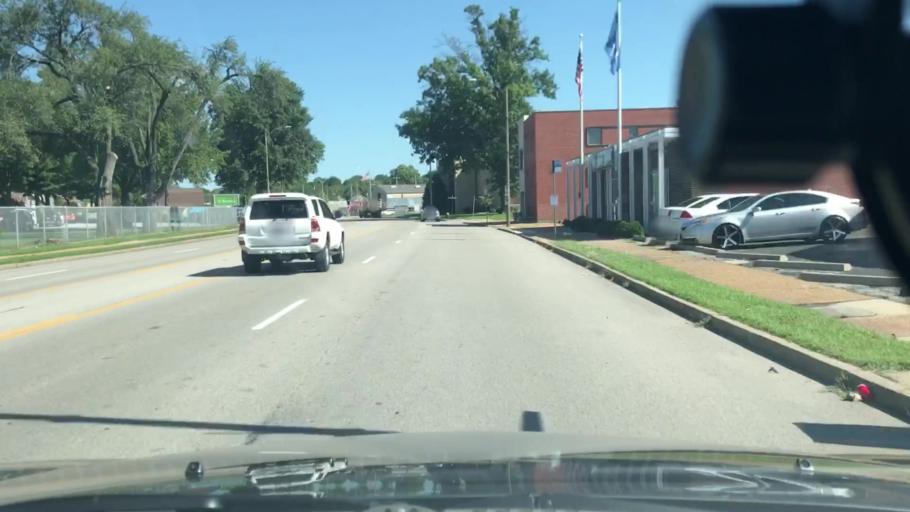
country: US
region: Missouri
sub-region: Saint Louis County
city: Maplewood
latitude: 38.5952
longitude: -90.2934
